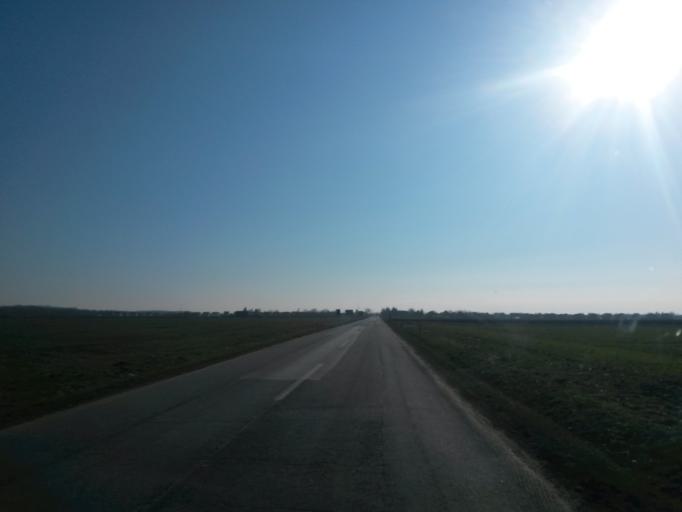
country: HR
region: Osjecko-Baranjska
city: Sarvas
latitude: 45.5323
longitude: 18.8198
